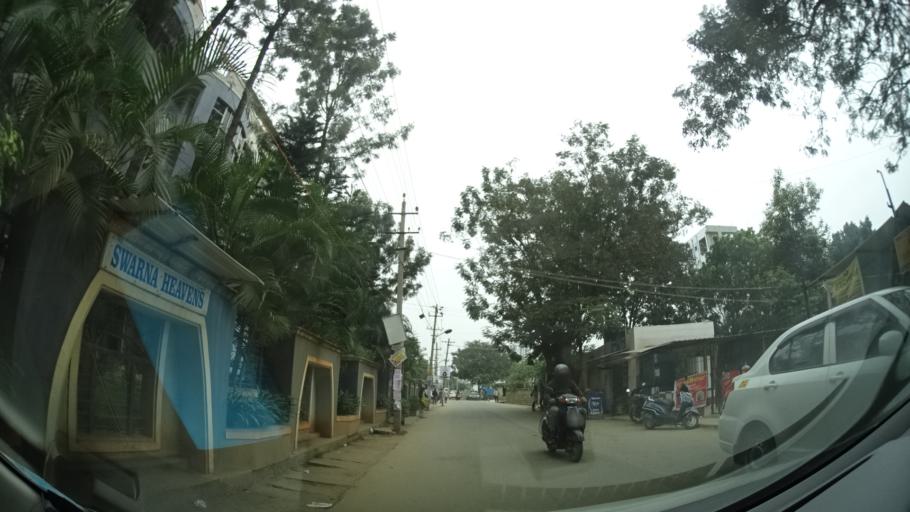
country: IN
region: Karnataka
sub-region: Bangalore Rural
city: Hoskote
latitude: 12.9829
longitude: 77.7473
